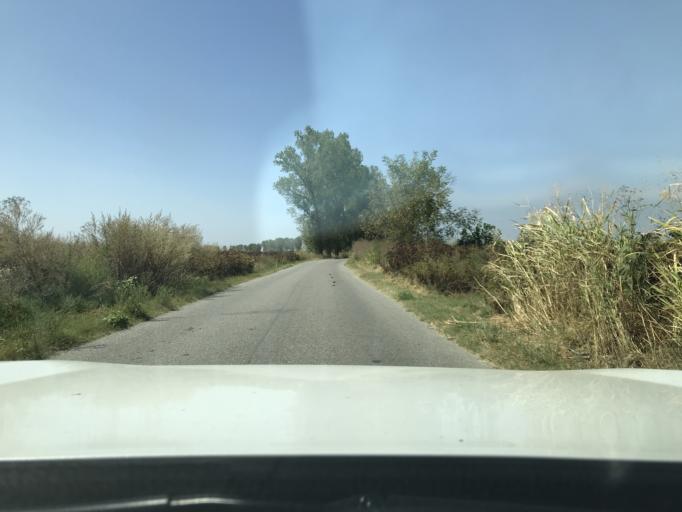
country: RO
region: Olt
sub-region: Comuna Falcoiu
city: Falcoiu
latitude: 44.2354
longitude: 24.3624
